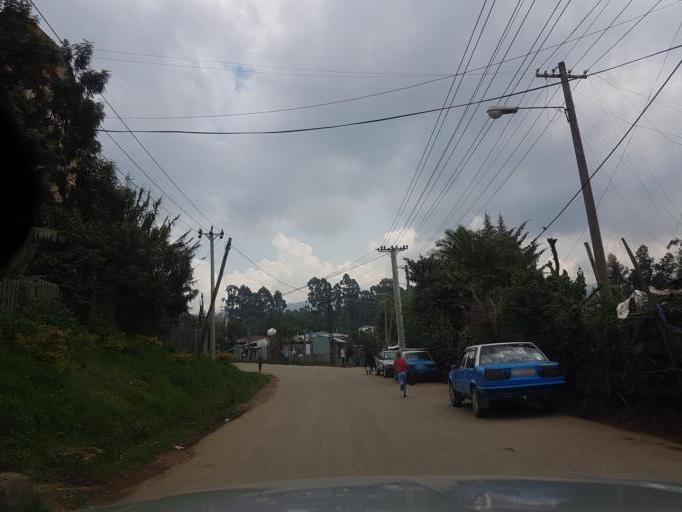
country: ET
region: Adis Abeba
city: Addis Ababa
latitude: 9.0240
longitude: 38.7680
